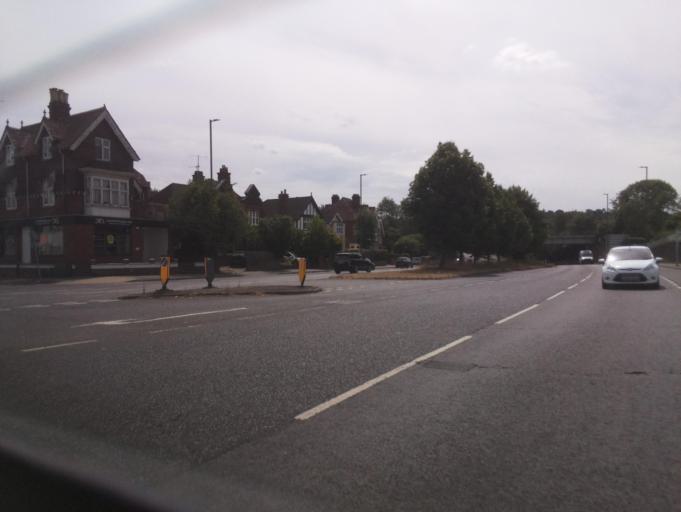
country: GB
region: England
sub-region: Surrey
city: Dorking
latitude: 51.2398
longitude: -0.3256
